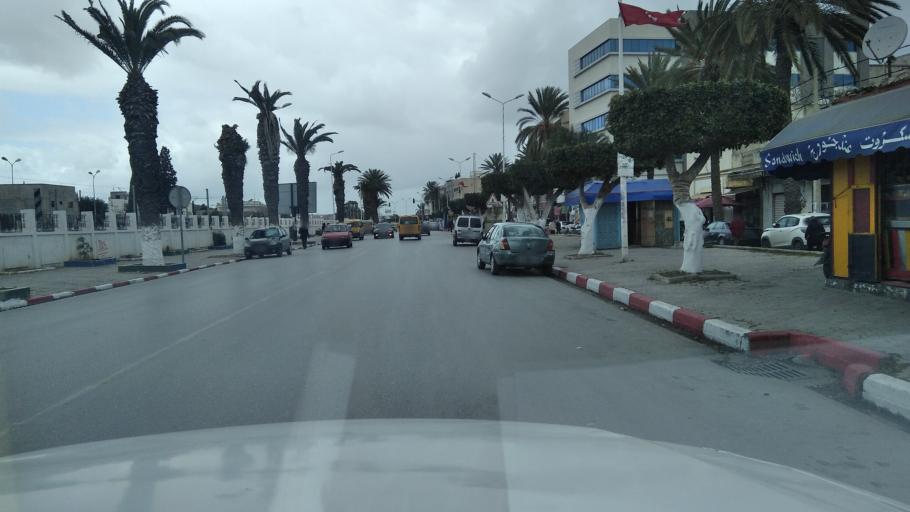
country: TN
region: Bin 'Arus
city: Ben Arous
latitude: 36.7551
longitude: 10.2213
